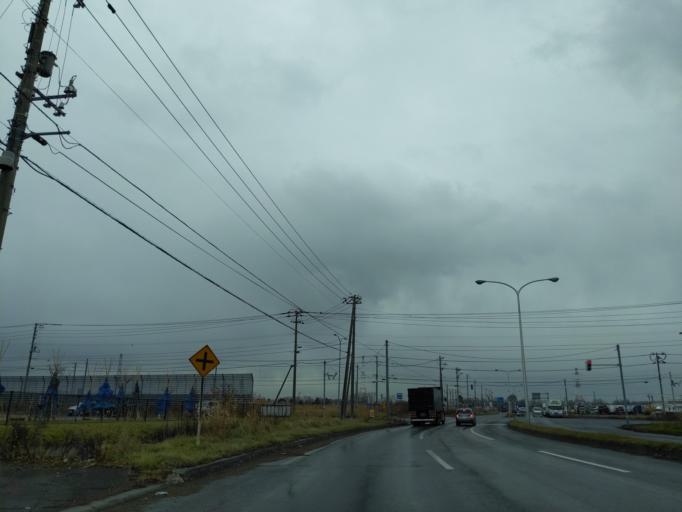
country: JP
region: Hokkaido
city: Ishikari
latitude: 43.1876
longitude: 141.3064
